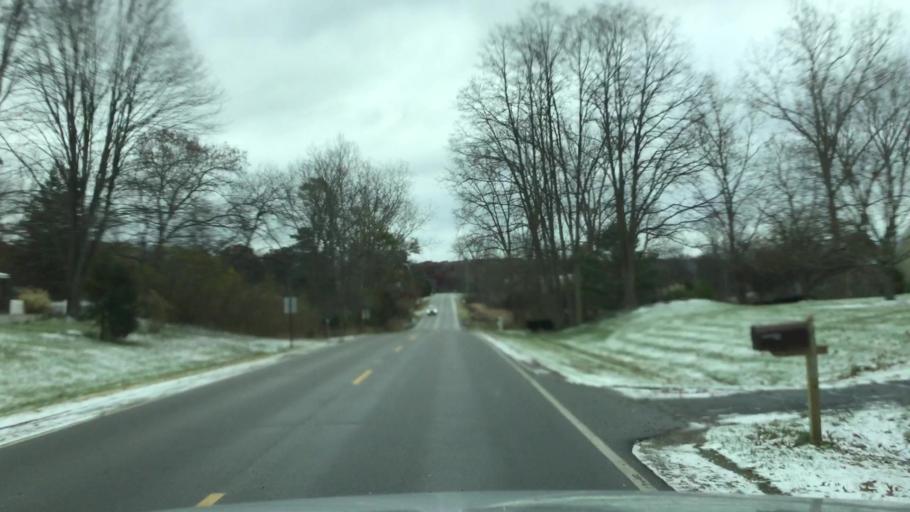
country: US
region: Michigan
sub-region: Livingston County
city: Brighton
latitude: 42.5386
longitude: -83.7257
